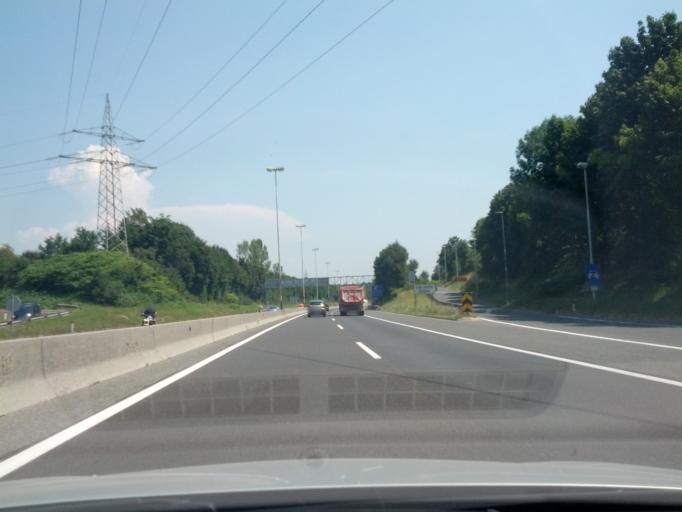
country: SI
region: Ljubljana
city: Ljubljana
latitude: 46.0820
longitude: 14.4891
